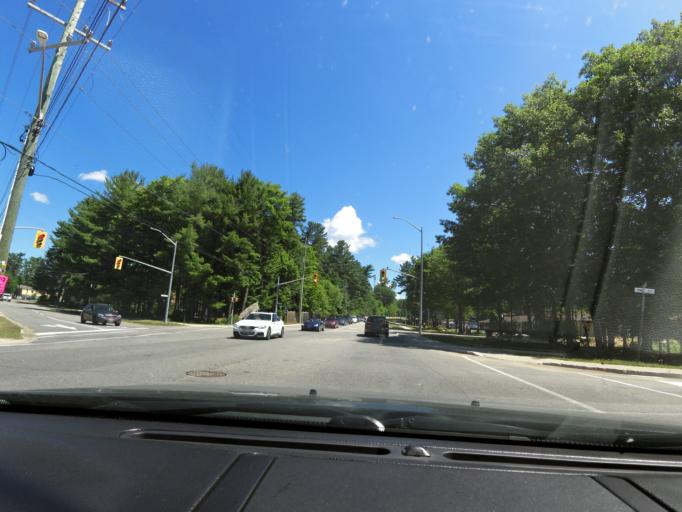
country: CA
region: Ontario
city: Bracebridge
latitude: 45.0490
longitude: -79.2981
